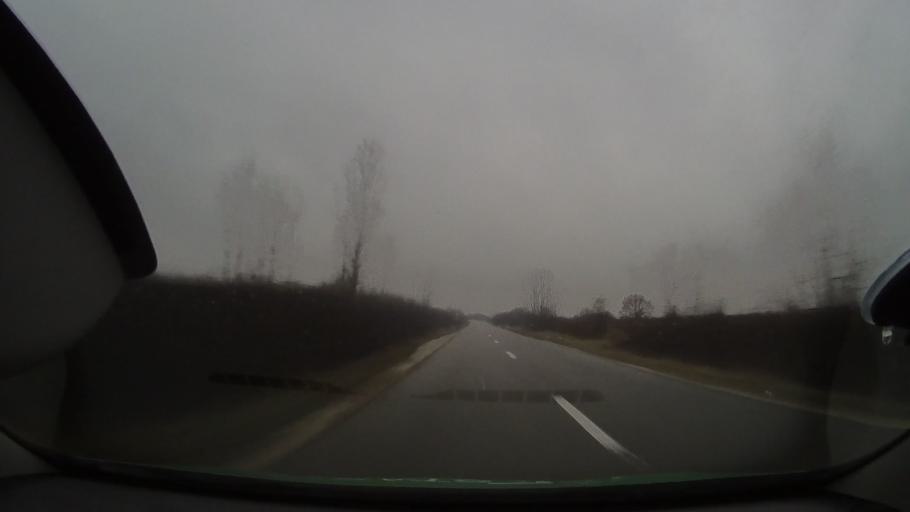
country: RO
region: Arad
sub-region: Comuna Craiova
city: Craiova
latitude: 46.5418
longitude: 21.9584
